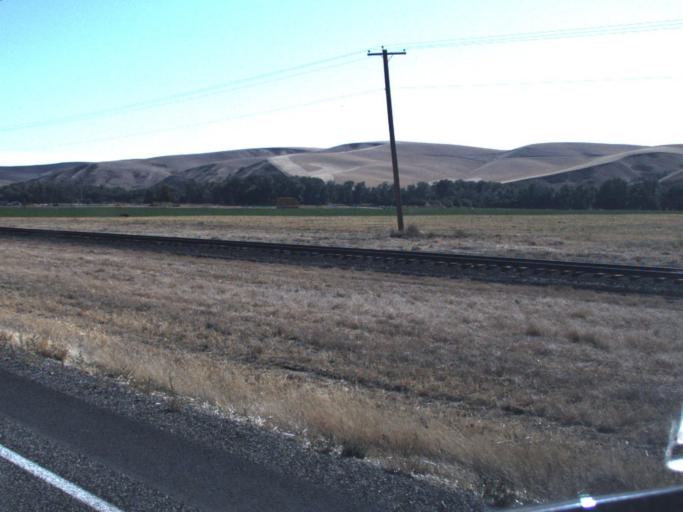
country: US
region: Washington
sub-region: Walla Walla County
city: Waitsburg
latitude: 46.2933
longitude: -118.2661
